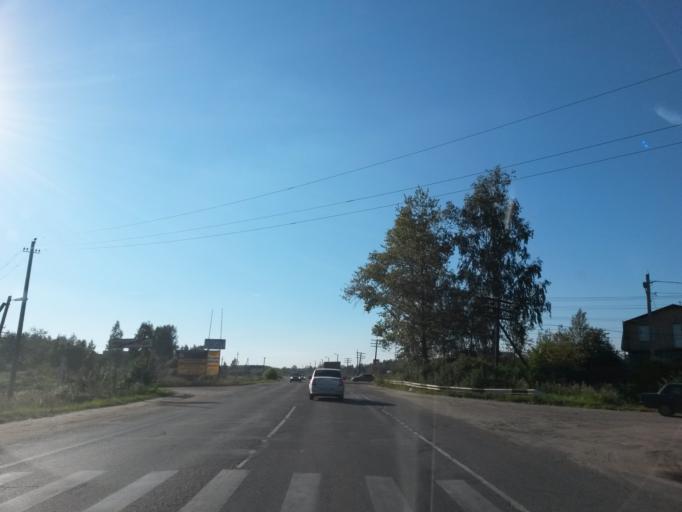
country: RU
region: Ivanovo
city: Novo-Talitsy
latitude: 57.0092
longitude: 40.8399
